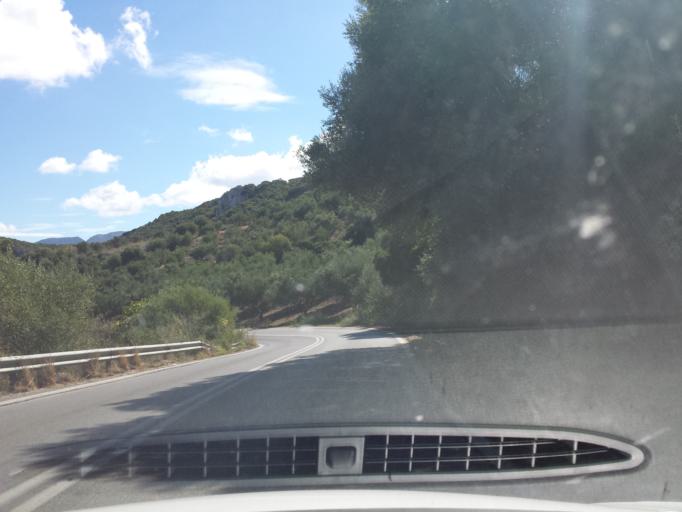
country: GR
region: Peloponnese
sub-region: Nomos Messinias
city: Pylos
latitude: 36.9316
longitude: 21.7313
